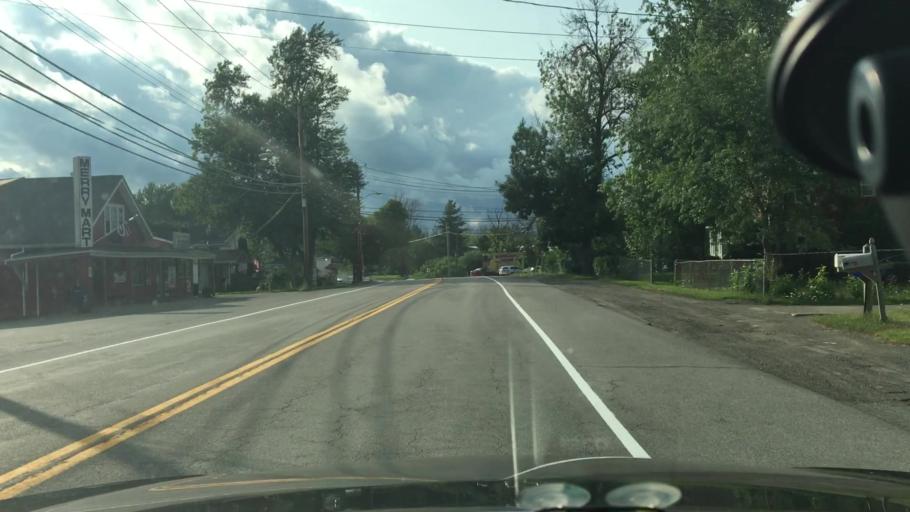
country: US
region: New York
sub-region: Erie County
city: Elma Center
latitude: 42.8217
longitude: -78.6814
